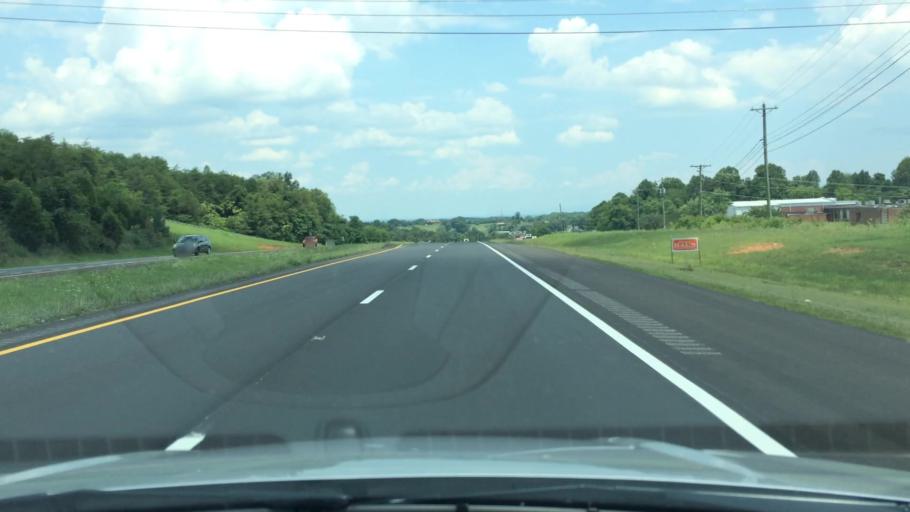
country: US
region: Tennessee
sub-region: Hamblen County
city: Morristown
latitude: 36.1828
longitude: -83.2464
